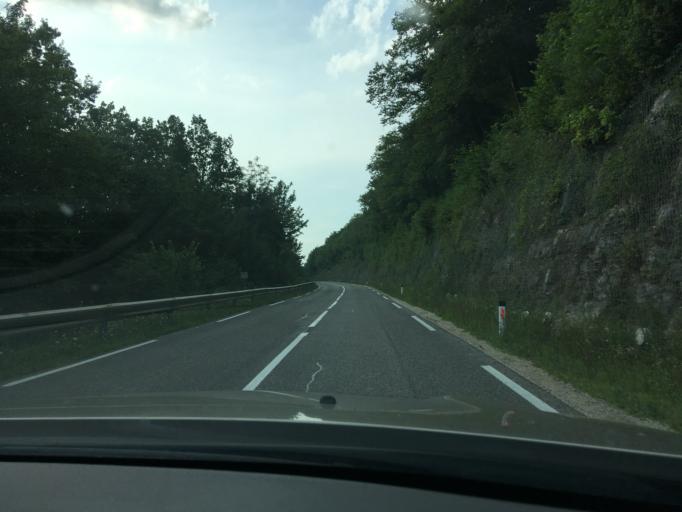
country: SI
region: Dolenjske Toplice
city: Dolenjske Toplice
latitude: 45.7883
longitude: 14.9913
